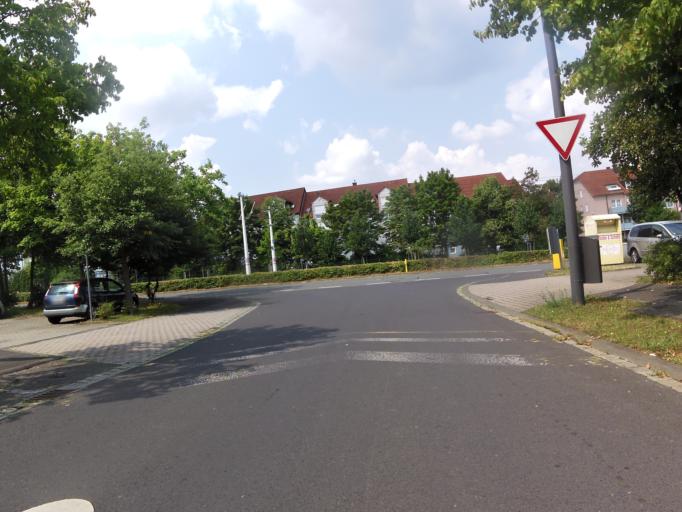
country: DE
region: Bavaria
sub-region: Regierungsbezirk Unterfranken
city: Randersacker
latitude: 49.7398
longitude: 9.9615
